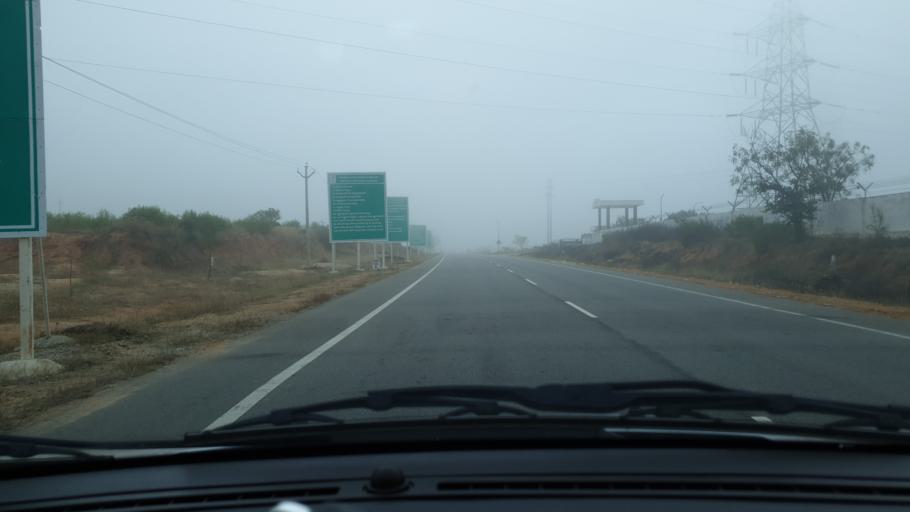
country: IN
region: Telangana
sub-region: Nalgonda
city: Devarkonda
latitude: 16.6160
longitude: 78.6741
